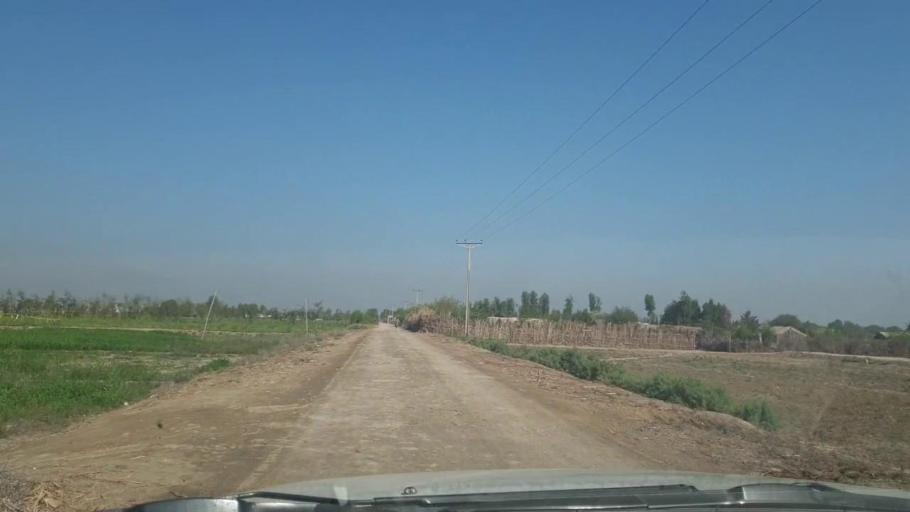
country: PK
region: Sindh
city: Mirpur Khas
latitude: 25.5024
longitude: 69.1586
